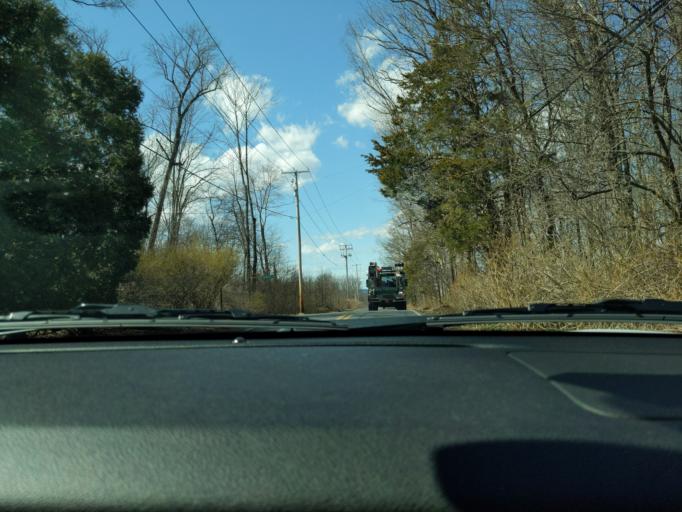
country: US
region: Pennsylvania
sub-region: Bucks County
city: Richlandtown
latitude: 40.4571
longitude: -75.2645
